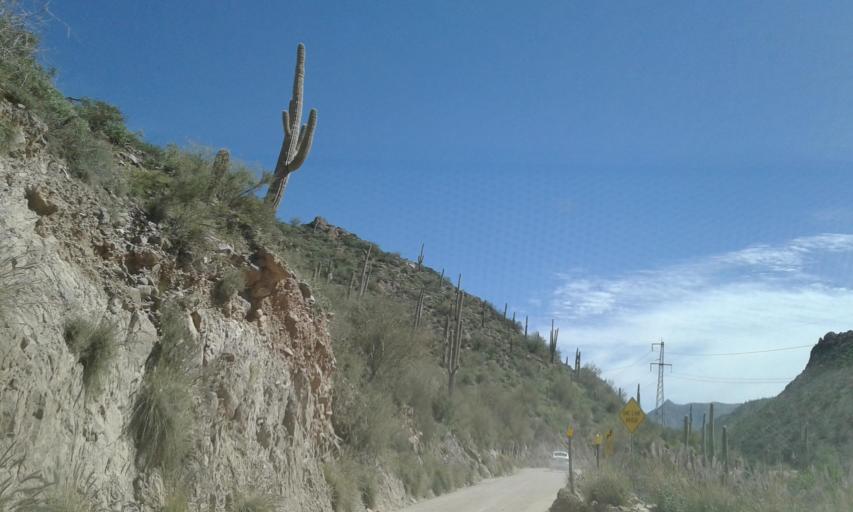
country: US
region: Arizona
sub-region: Pinal County
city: Gold Camp
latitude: 33.5386
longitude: -111.2889
